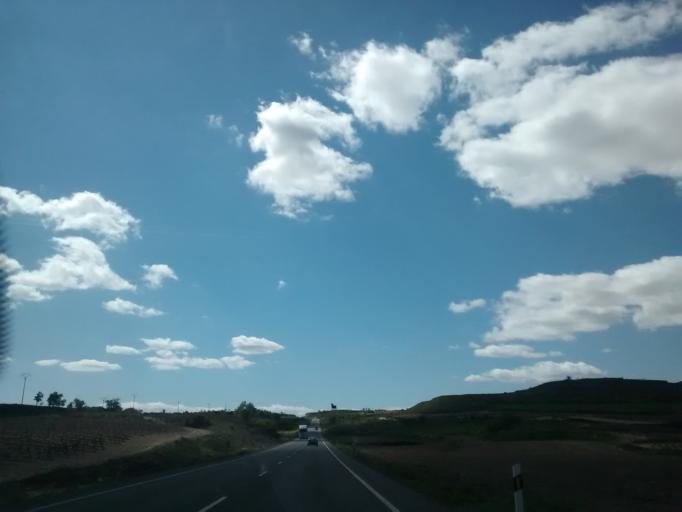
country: ES
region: La Rioja
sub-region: Provincia de La Rioja
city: Torremontalbo
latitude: 42.5088
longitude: -2.7078
